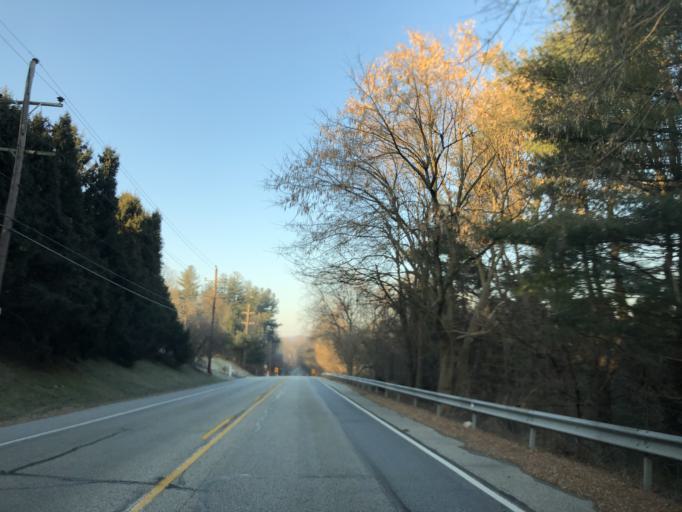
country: US
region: Pennsylvania
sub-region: Chester County
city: West Chester
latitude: 39.9682
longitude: -75.6519
